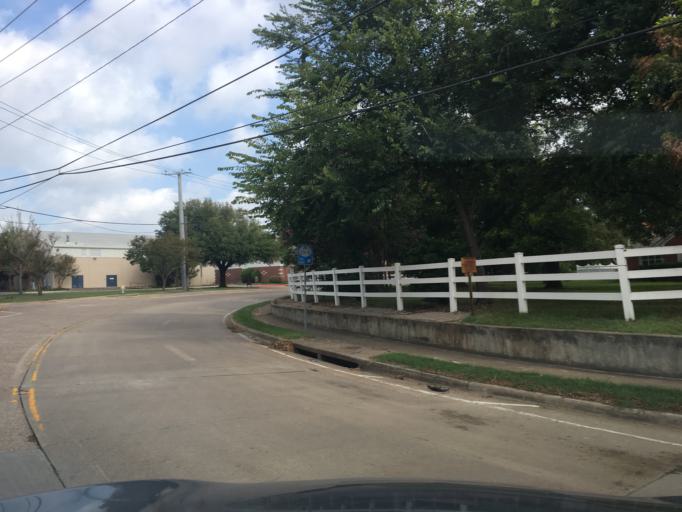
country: US
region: Texas
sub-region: Dallas County
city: Richardson
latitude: 32.9049
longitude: -96.7603
